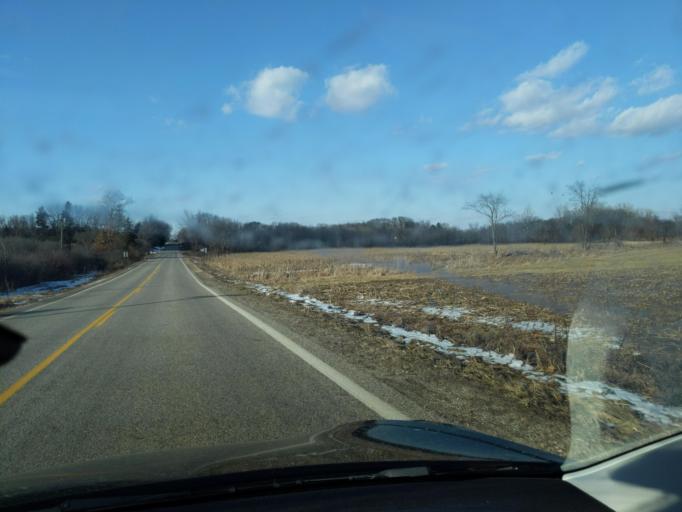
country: US
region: Michigan
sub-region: Ingham County
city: Stockbridge
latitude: 42.4870
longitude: -84.0861
